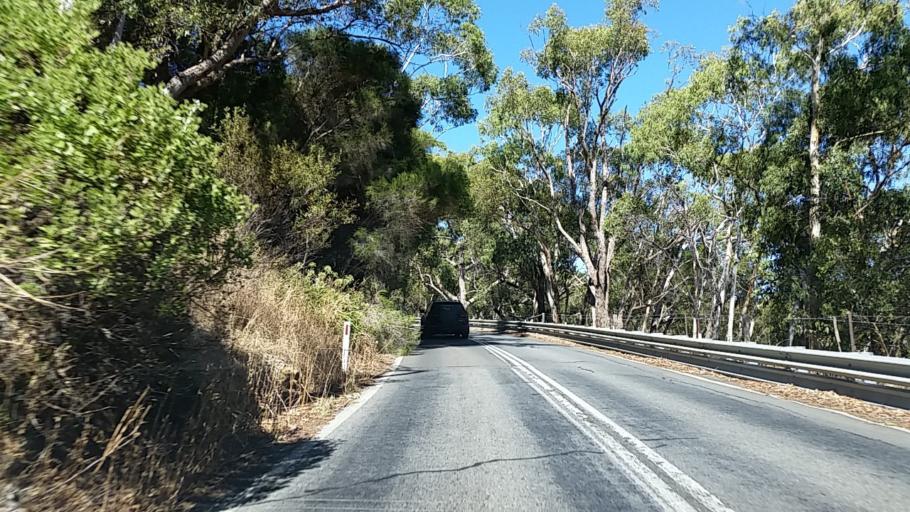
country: AU
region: South Australia
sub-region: Burnside
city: Beaumont
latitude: -34.9539
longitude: 138.6978
